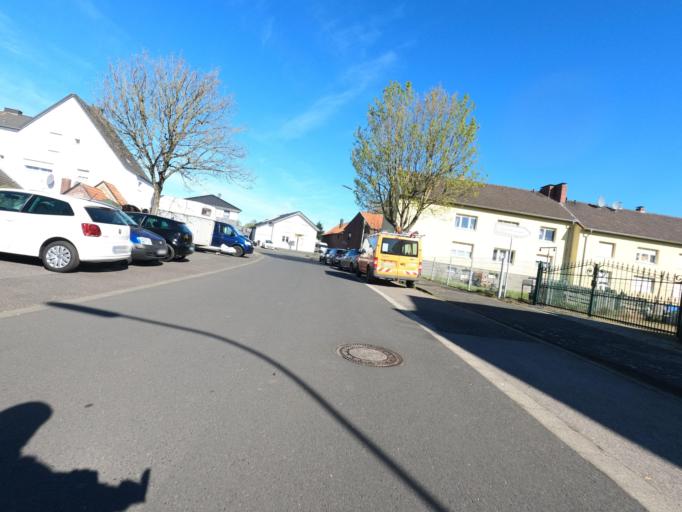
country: DE
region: North Rhine-Westphalia
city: Huckelhoven
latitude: 51.0663
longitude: 6.2150
